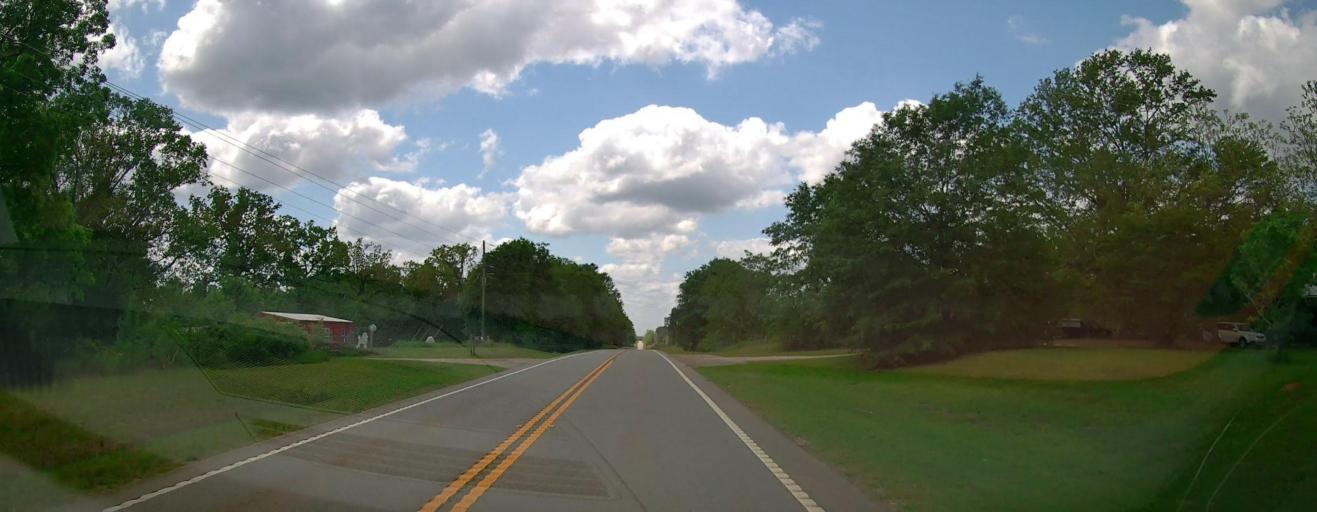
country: US
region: Georgia
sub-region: Laurens County
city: Dublin
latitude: 32.5737
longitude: -83.0269
